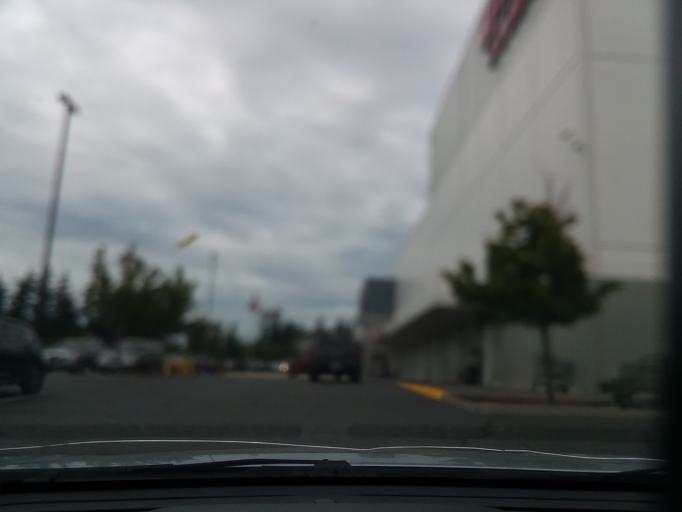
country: US
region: Washington
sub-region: Whatcom County
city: Bellingham
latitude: 48.7863
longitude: -122.4821
